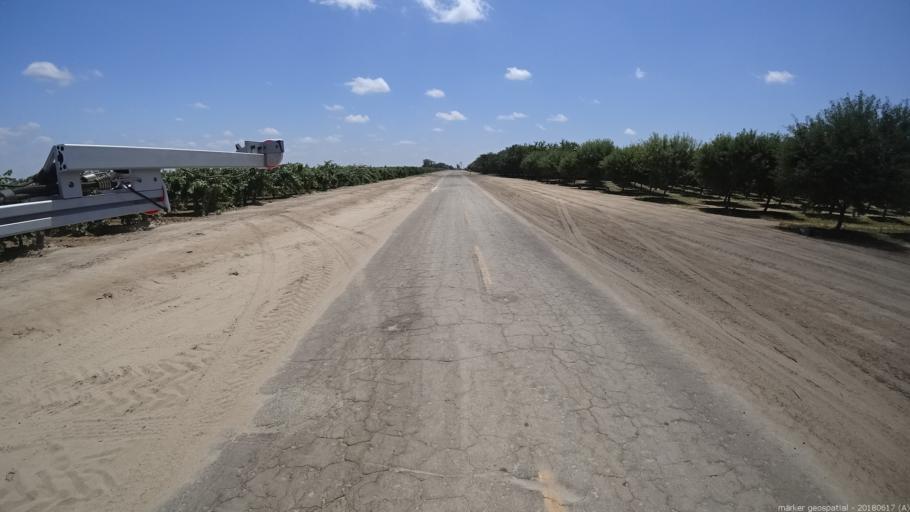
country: US
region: California
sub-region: Fresno County
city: Biola
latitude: 36.8268
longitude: -120.1330
